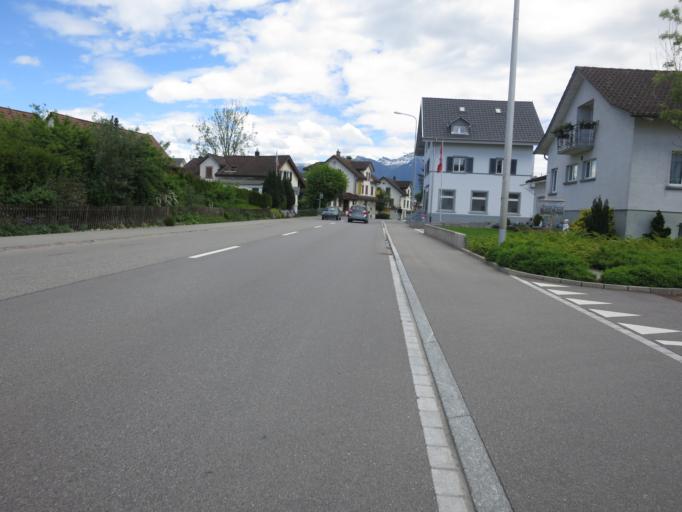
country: CH
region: Schwyz
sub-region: Bezirk March
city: Schubelbach
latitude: 47.1753
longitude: 8.9481
